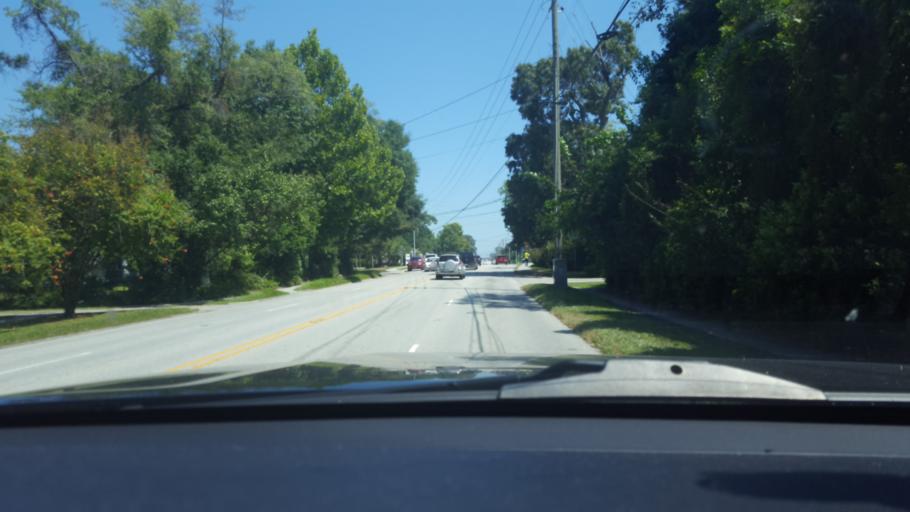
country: US
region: North Carolina
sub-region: New Hanover County
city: Wilmington
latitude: 34.2389
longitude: -77.9128
